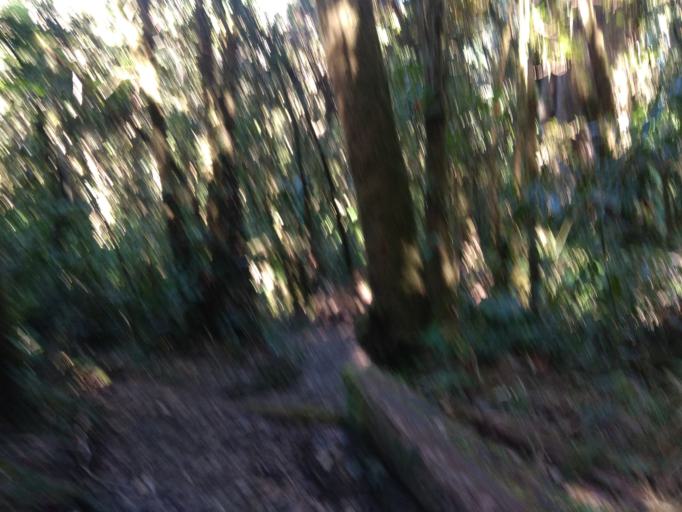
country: CR
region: Heredia
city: Santo Domingo
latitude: 10.1331
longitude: -84.1152
